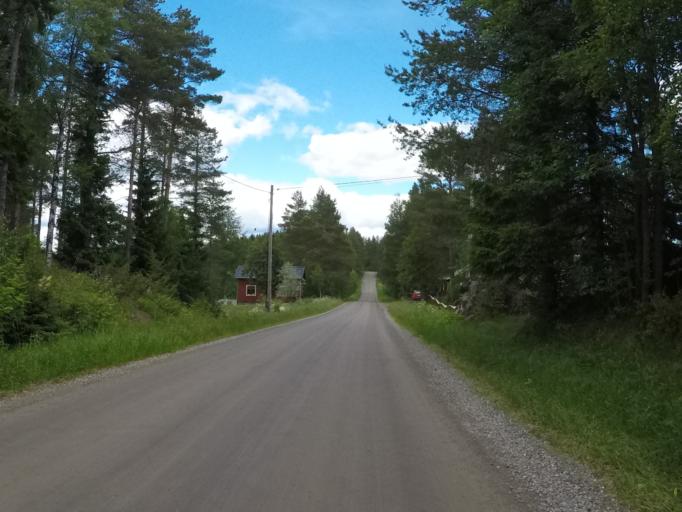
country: SE
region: Vaesterbotten
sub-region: Robertsfors Kommun
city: Robertsfors
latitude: 64.1569
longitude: 20.9180
